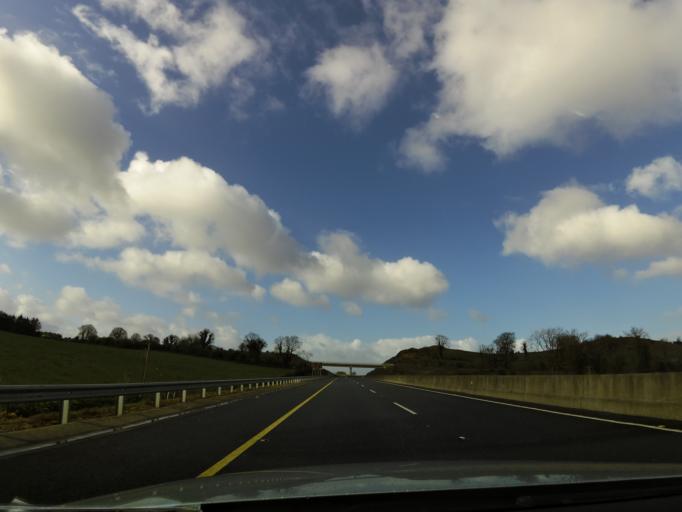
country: IE
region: Munster
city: Ballina
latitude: 52.7729
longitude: -8.3824
